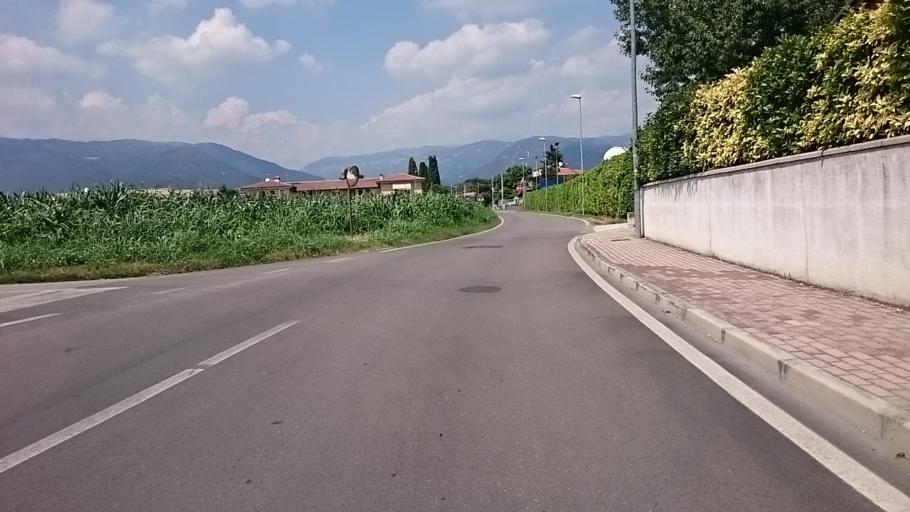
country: IT
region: Veneto
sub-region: Provincia di Vicenza
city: Bassano del Grappa
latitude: 45.7469
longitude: 11.7304
